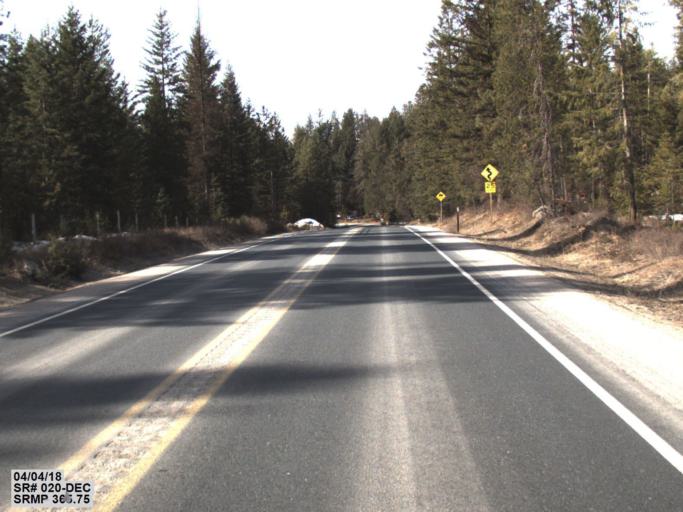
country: US
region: Washington
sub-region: Stevens County
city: Colville
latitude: 48.5084
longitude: -117.7047
